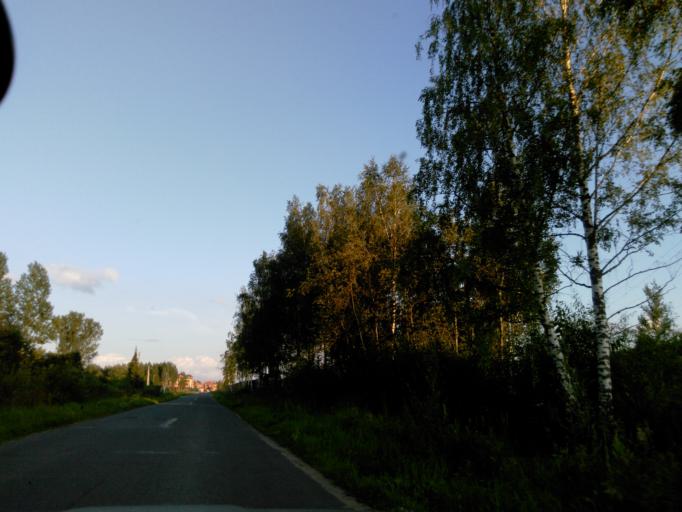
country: RU
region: Tverskaya
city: Konakovo
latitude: 56.6811
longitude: 36.7050
